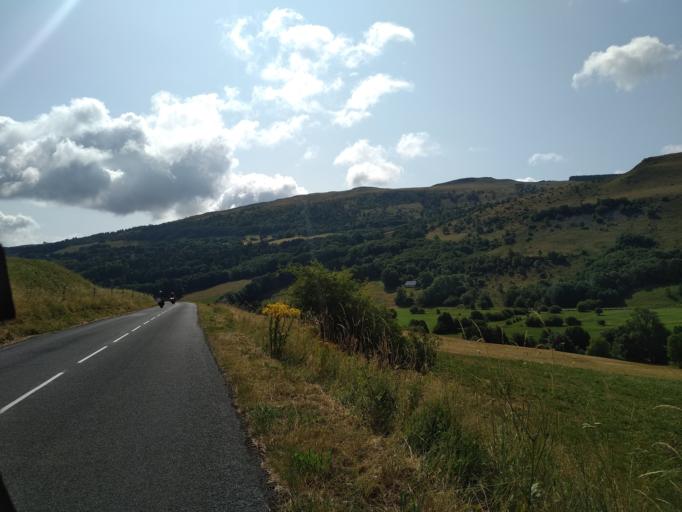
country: FR
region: Auvergne
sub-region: Departement du Cantal
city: Murat
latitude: 45.1426
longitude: 2.7625
